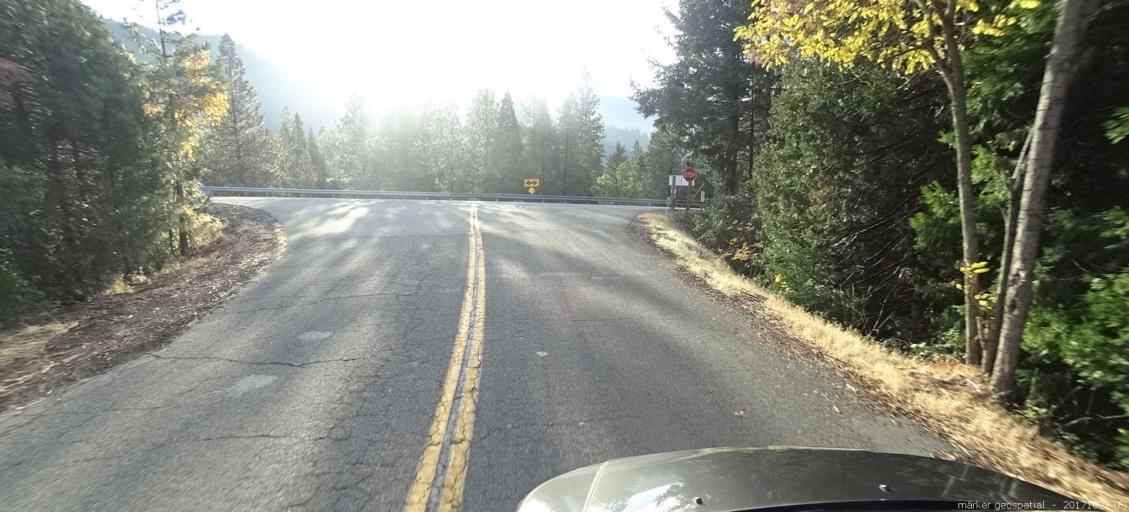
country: US
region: California
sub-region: Siskiyou County
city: Dunsmuir
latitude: 41.1833
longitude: -122.2917
